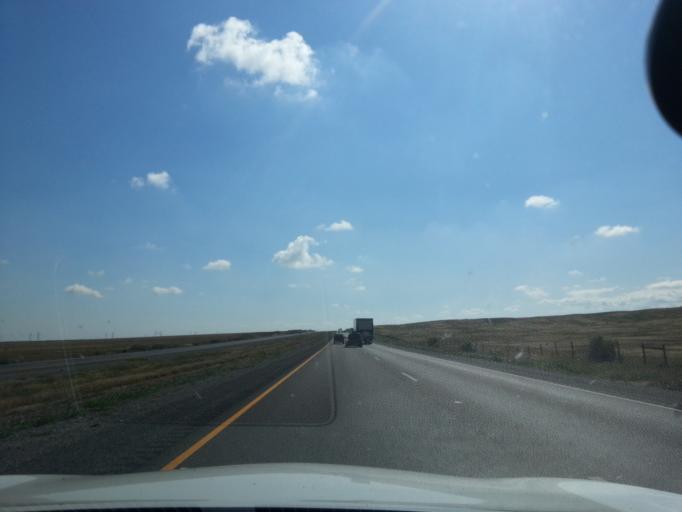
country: US
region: California
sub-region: Fresno County
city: Mendota
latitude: 36.5411
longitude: -120.5018
